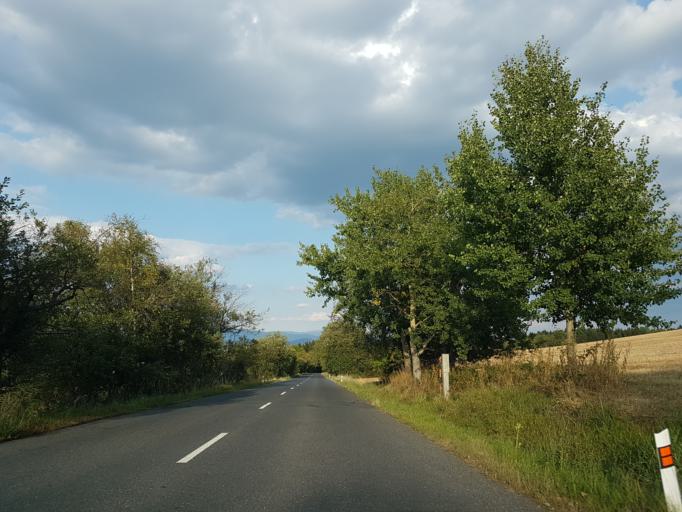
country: CZ
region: Liberecky
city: Mala Skala
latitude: 50.6653
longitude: 15.1733
